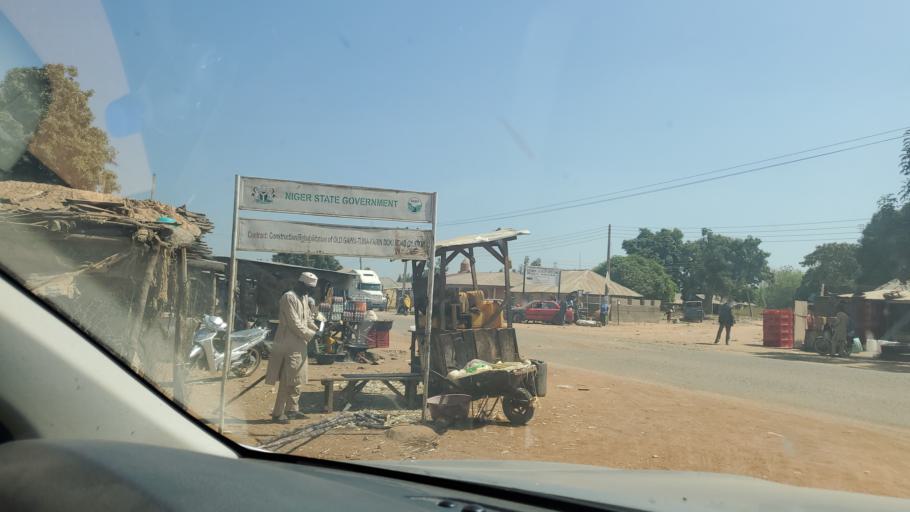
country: NG
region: Niger
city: Gawu Babangida
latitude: 9.2130
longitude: 6.8433
